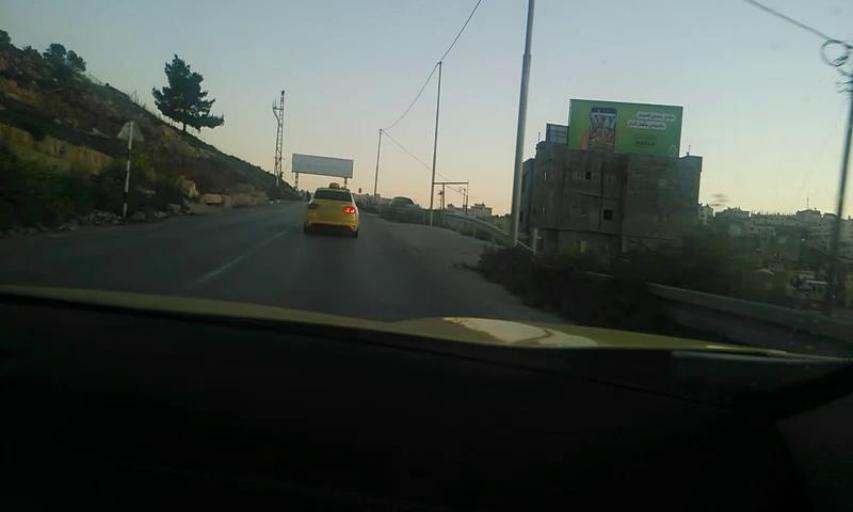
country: PS
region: West Bank
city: Jifna
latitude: 31.9515
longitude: 35.2149
